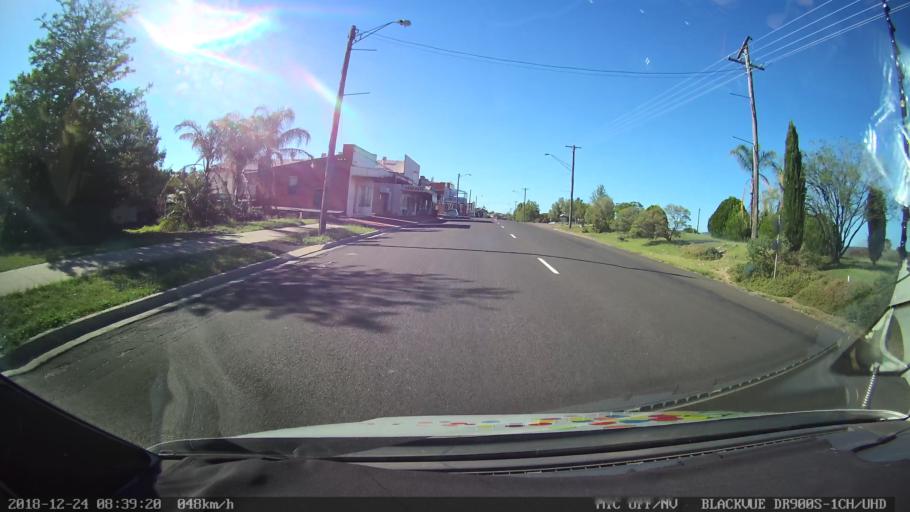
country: AU
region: New South Wales
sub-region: Liverpool Plains
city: Quirindi
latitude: -31.3473
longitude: 150.6473
